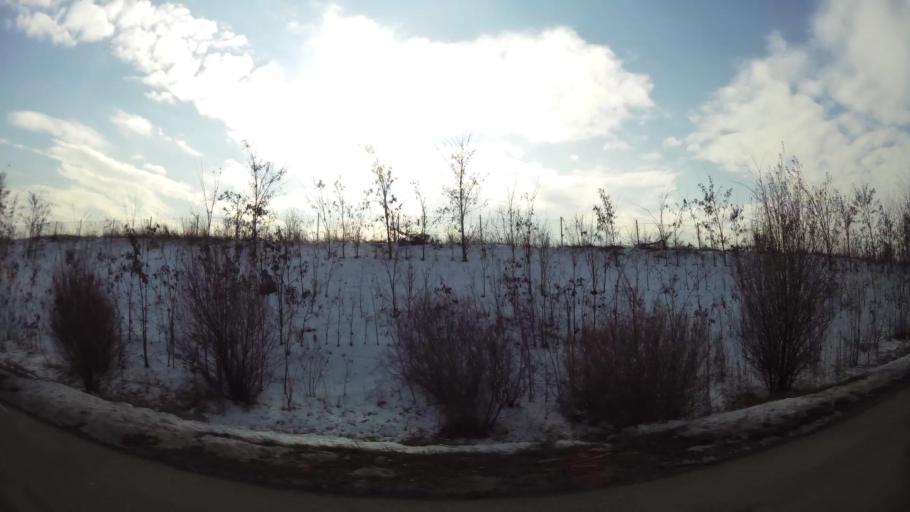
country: MK
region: Suto Orizari
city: Suto Orizare
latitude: 42.0490
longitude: 21.4337
